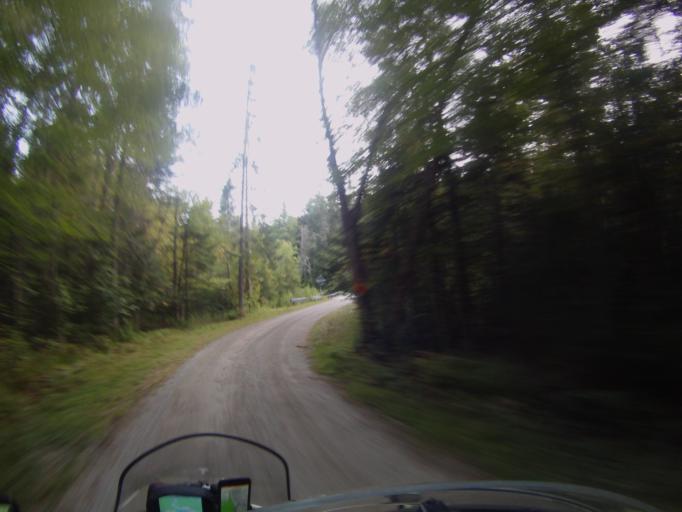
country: US
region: Vermont
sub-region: Addison County
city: Bristol
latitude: 44.0047
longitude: -73.0193
